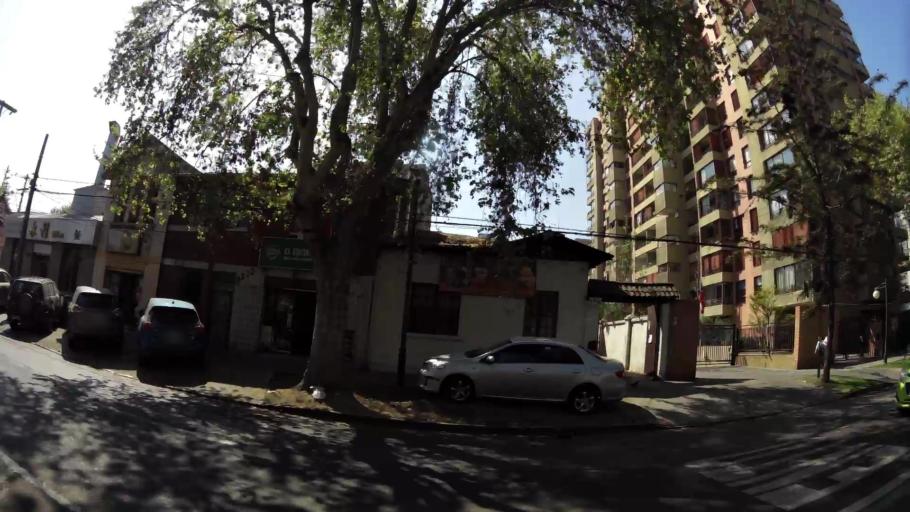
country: CL
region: Santiago Metropolitan
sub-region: Provincia de Santiago
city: Santiago
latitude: -33.4561
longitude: -70.6156
